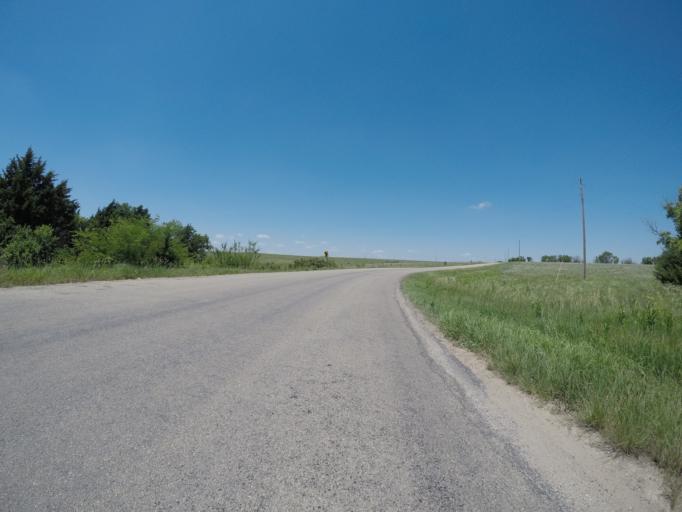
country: US
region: Kansas
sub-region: Geary County
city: Grandview Plaza
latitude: 38.8683
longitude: -96.7978
